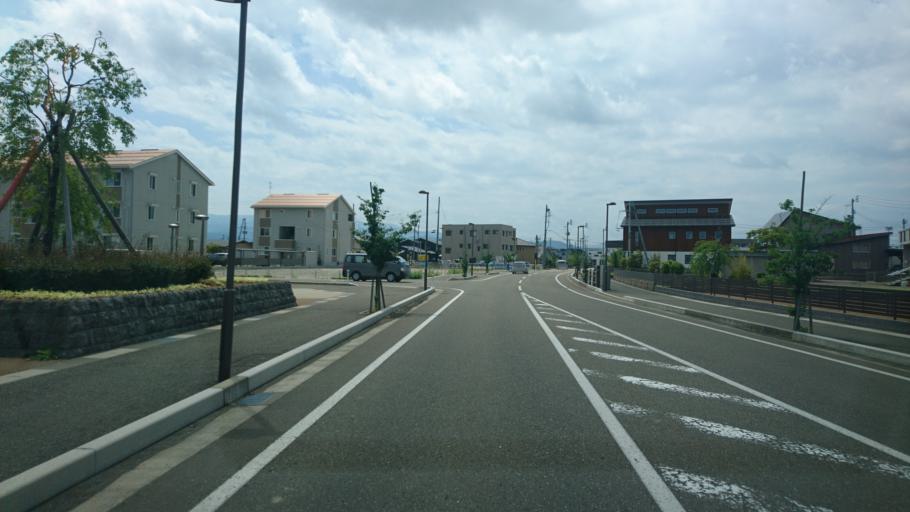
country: JP
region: Niigata
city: Joetsu
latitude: 37.0804
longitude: 138.2466
